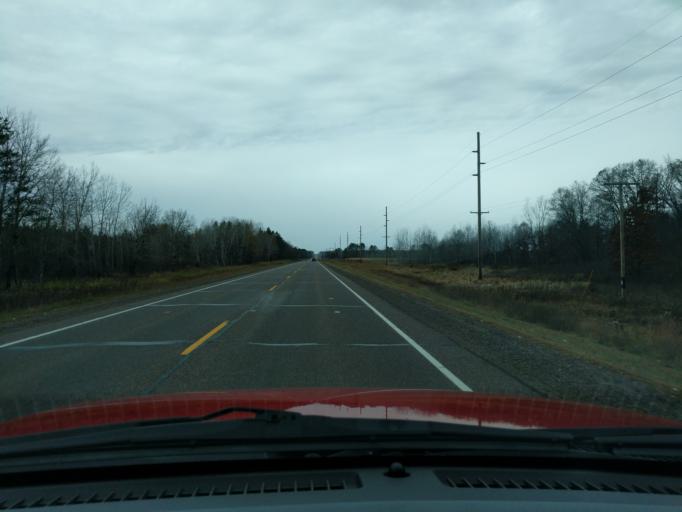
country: US
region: Wisconsin
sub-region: Washburn County
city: Shell Lake
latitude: 45.8151
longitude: -91.9860
